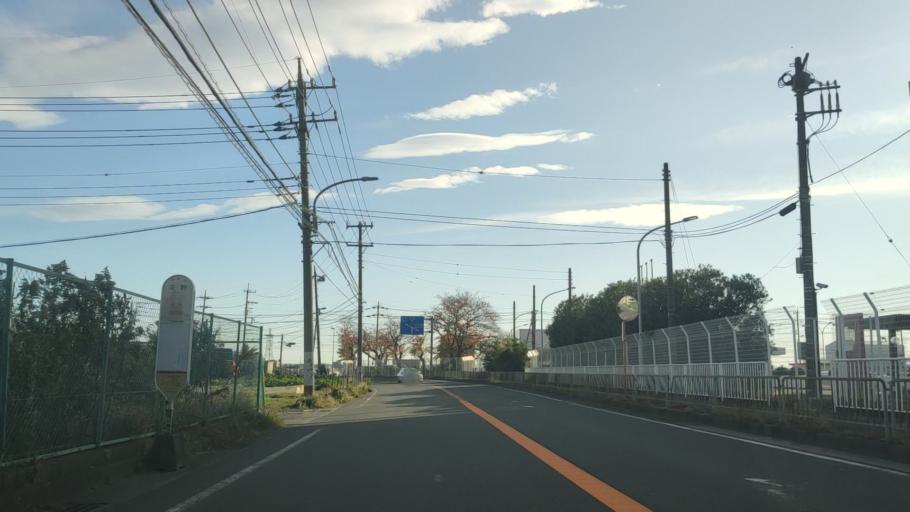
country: JP
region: Kanagawa
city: Atsugi
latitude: 35.4227
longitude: 139.3876
